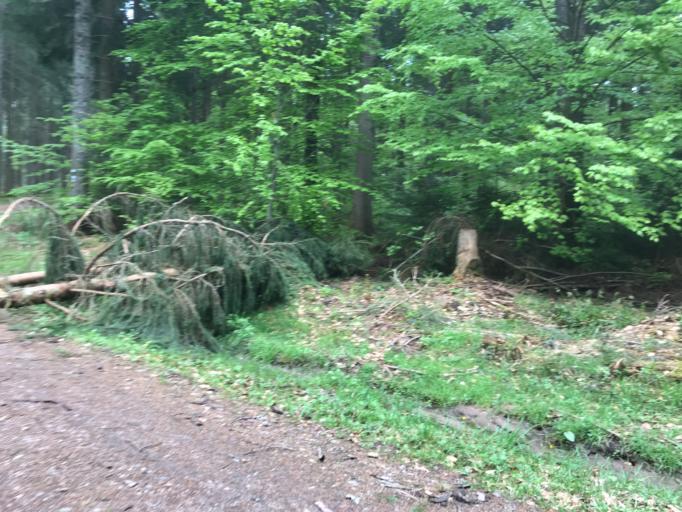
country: DE
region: Baden-Wuerttemberg
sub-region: Karlsruhe Region
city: Baiersbronn
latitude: 48.4824
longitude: 8.3303
